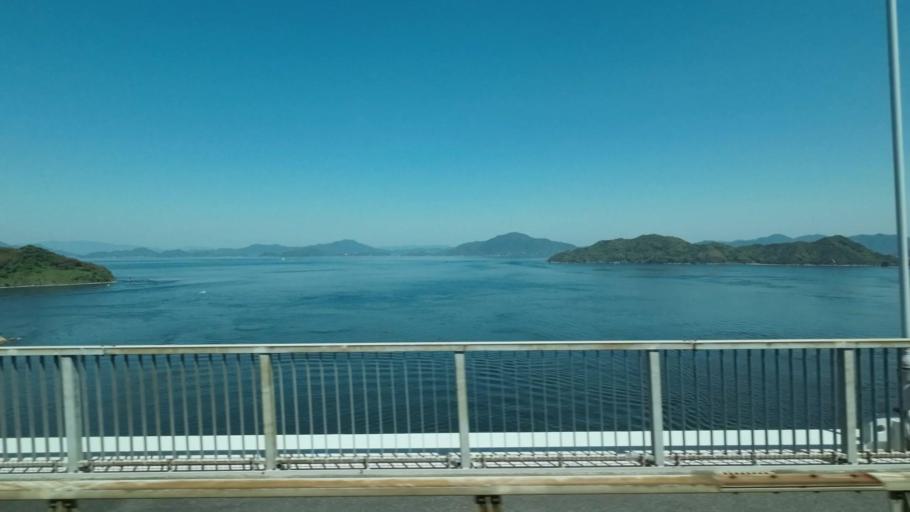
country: JP
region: Hiroshima
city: Takehara
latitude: 34.1202
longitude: 132.9990
